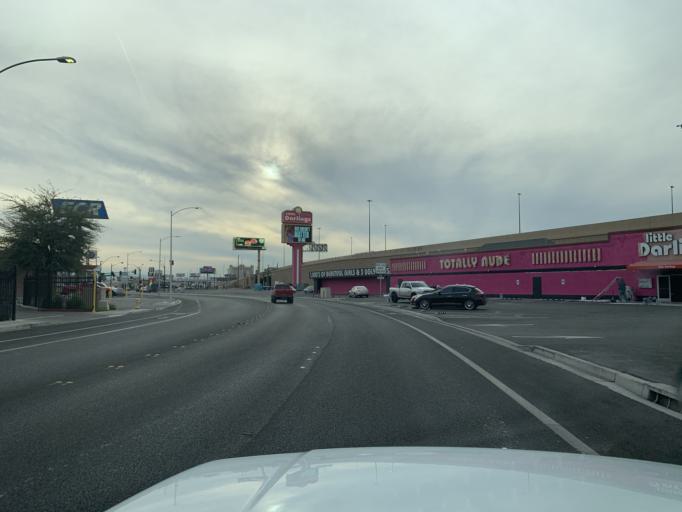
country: US
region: Nevada
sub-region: Clark County
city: Las Vegas
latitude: 36.1539
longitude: -115.1608
